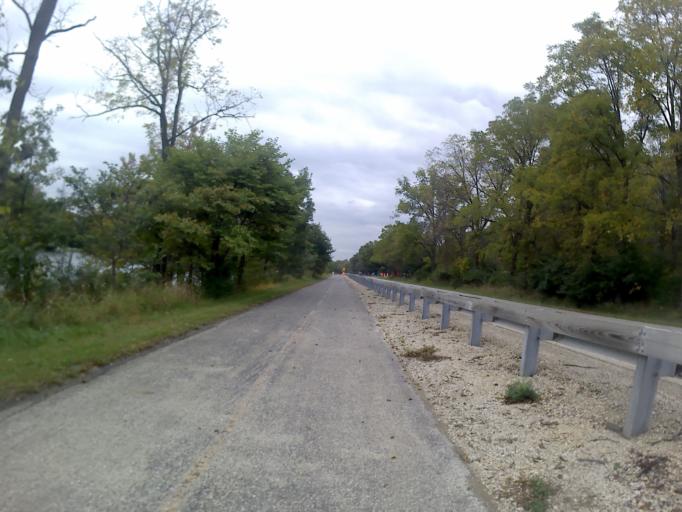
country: US
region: Illinois
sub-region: Kendall County
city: Boulder Hill
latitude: 41.7063
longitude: -88.3504
